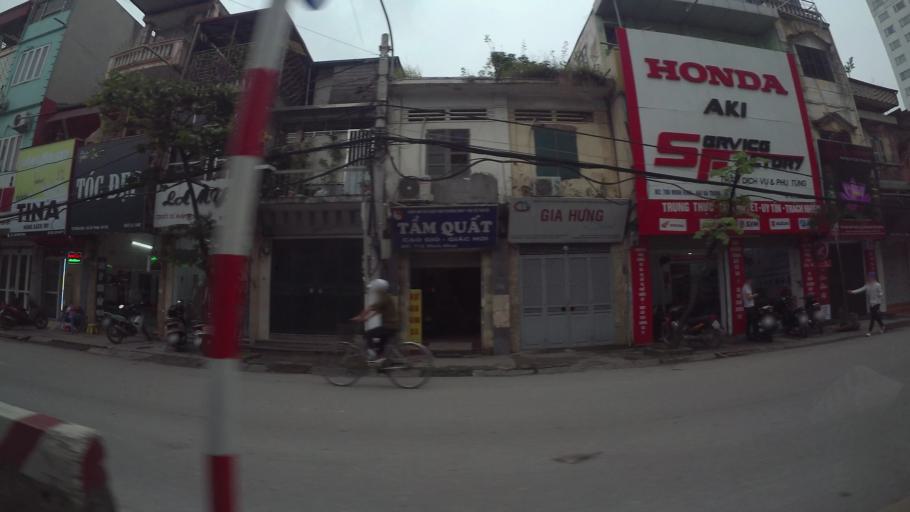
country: VN
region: Ha Noi
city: Hai BaTrung
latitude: 21.0014
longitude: 105.8704
